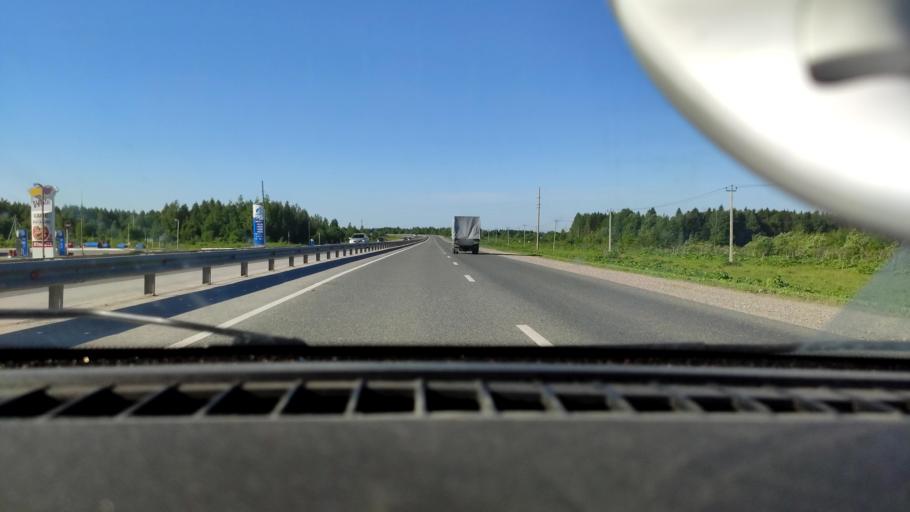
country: RU
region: Perm
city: Polazna
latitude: 58.2110
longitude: 56.4052
